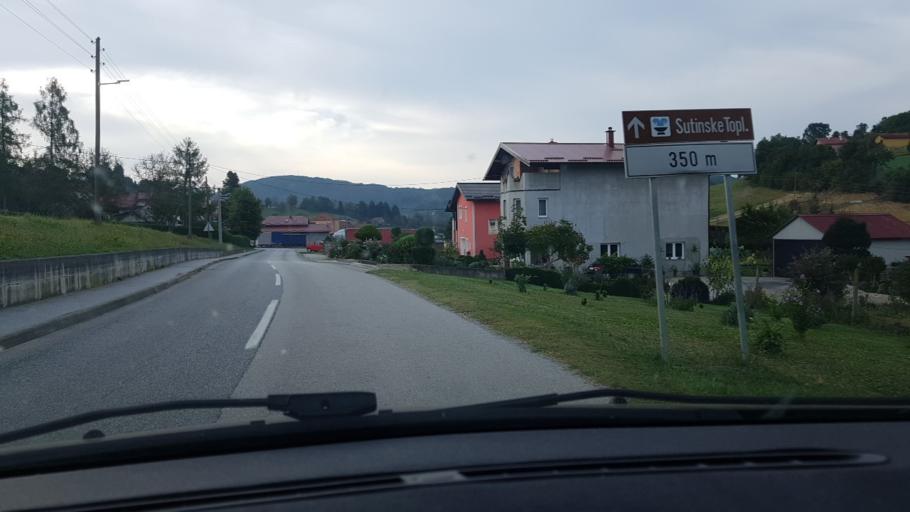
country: HR
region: Krapinsko-Zagorska
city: Mihovljan
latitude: 46.1365
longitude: 15.9666
